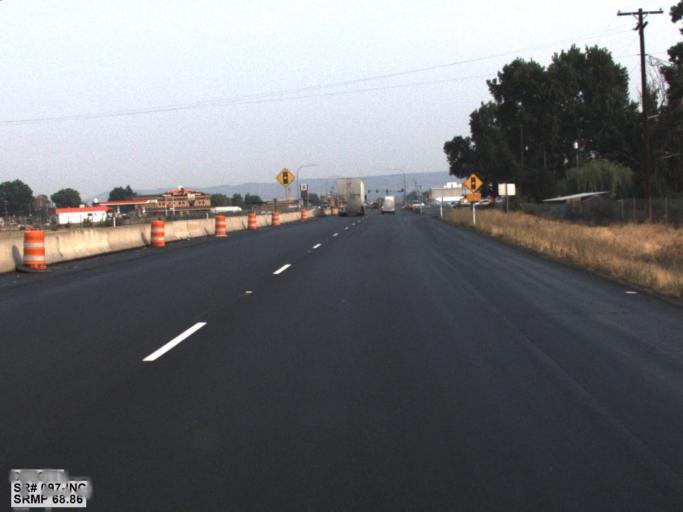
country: US
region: Washington
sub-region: Yakima County
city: Wapato
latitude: 46.4445
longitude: -120.4301
